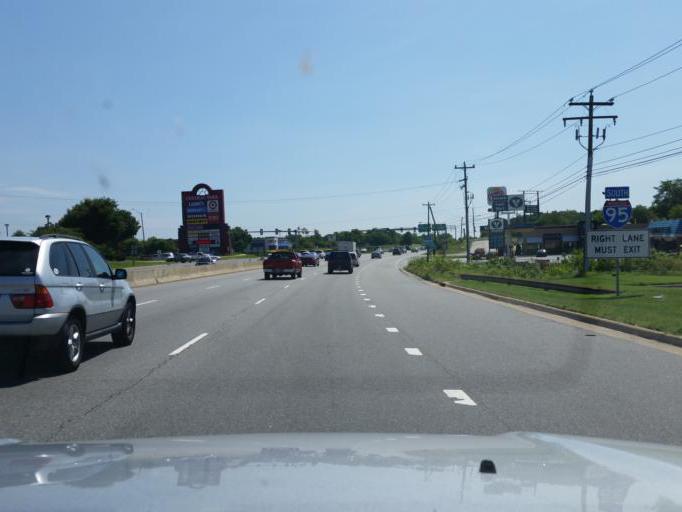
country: US
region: Virginia
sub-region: Stafford County
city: Falmouth
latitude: 38.2955
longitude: -77.5144
